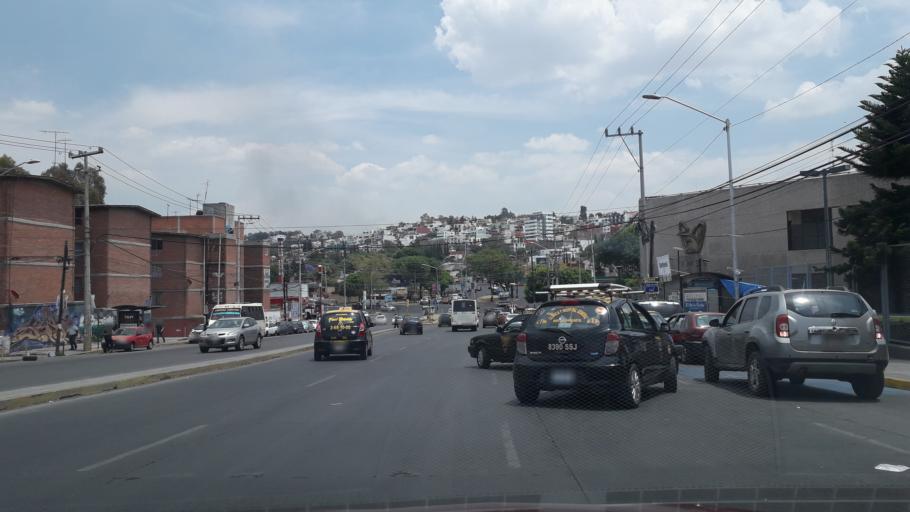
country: MX
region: Puebla
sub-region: Puebla
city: Galaxia la Calera
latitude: 19.0093
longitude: -98.1827
